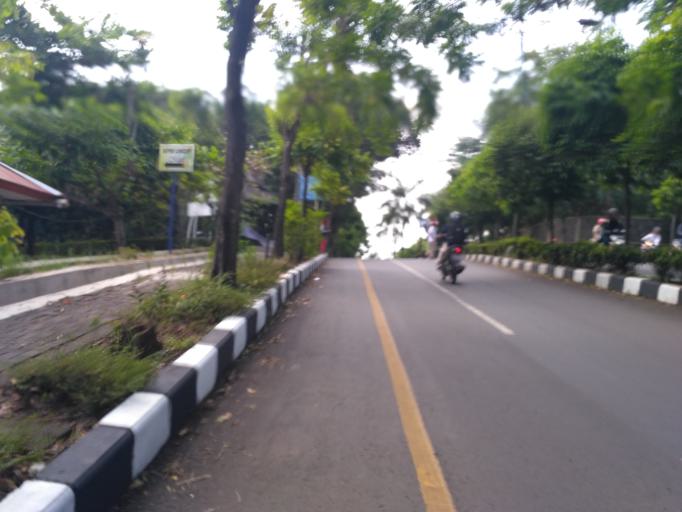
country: ID
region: Central Java
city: Semarang
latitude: -7.0539
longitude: 110.4395
